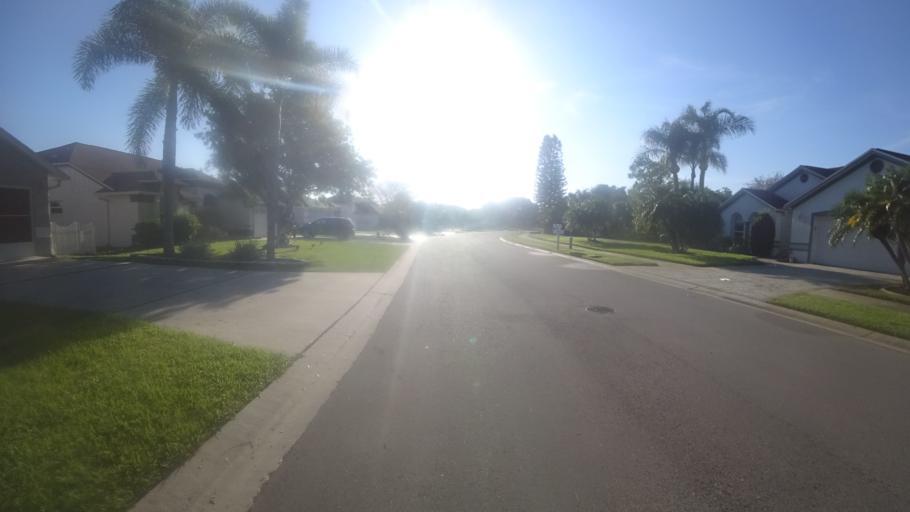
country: US
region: Florida
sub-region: Manatee County
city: Ellenton
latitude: 27.4890
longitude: -82.5059
